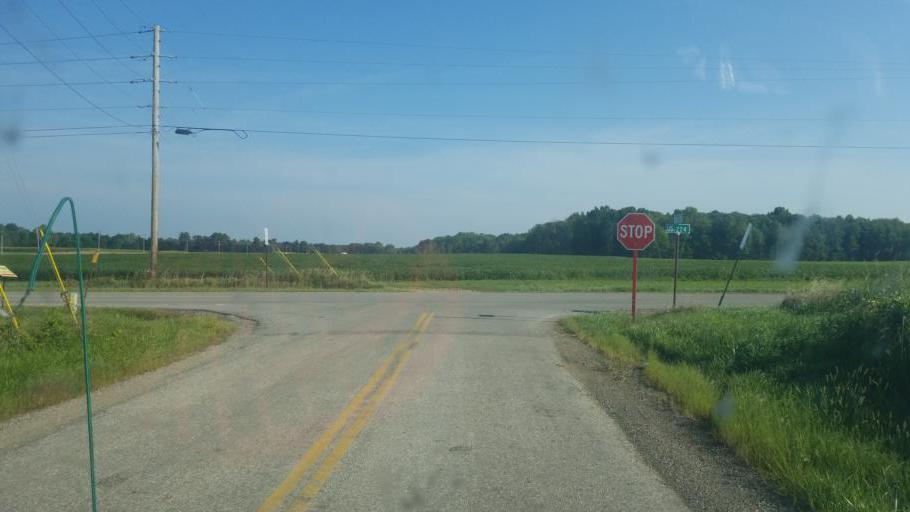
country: US
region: Ohio
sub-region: Huron County
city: New London
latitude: 41.0294
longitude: -82.3541
